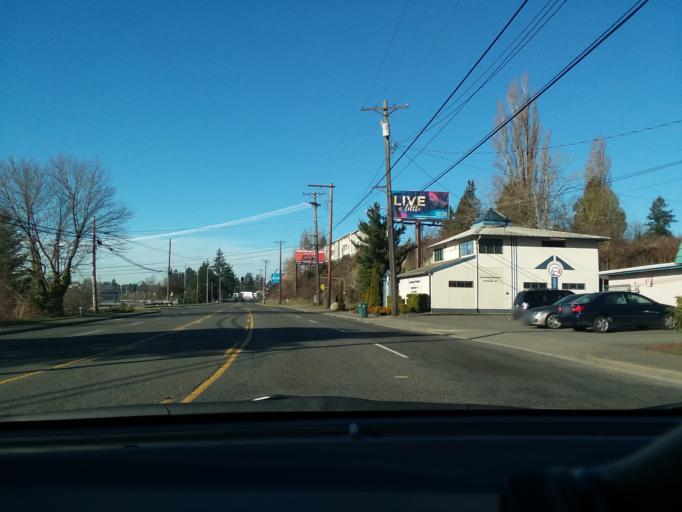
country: US
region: Washington
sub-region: Pierce County
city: Fircrest
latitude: 47.2332
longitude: -122.4781
